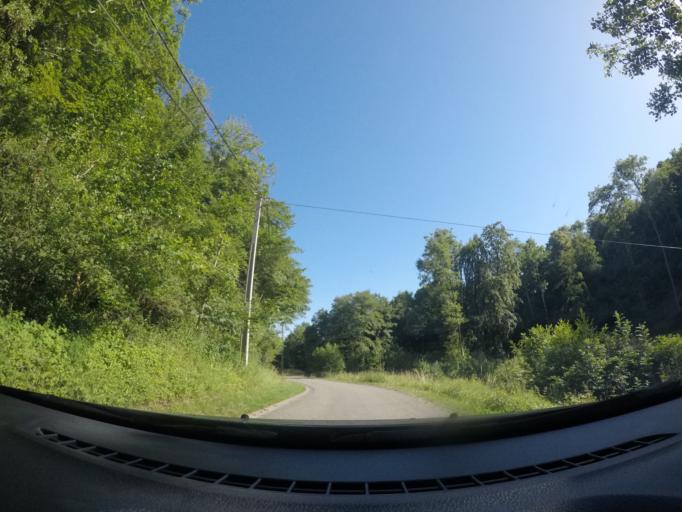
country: BE
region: Wallonia
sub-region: Province de Namur
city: Philippeville
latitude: 50.1694
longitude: 4.5561
